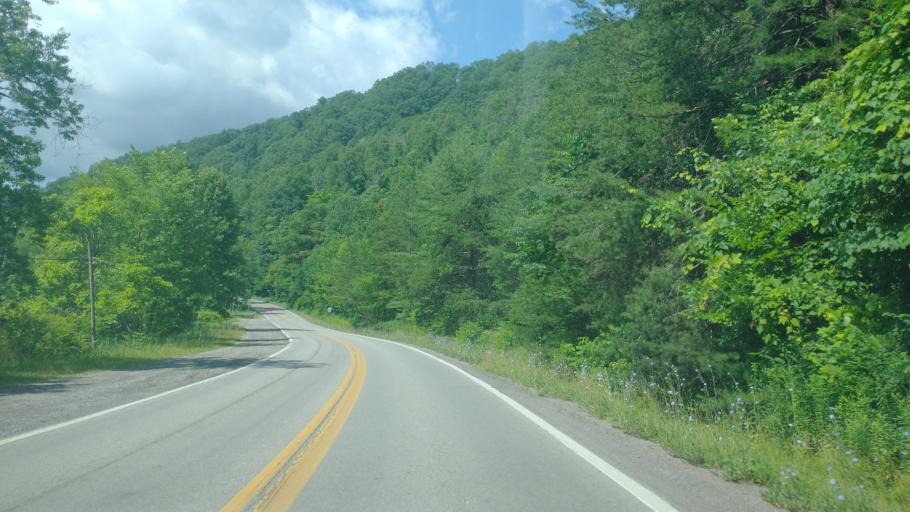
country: US
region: West Virginia
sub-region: McDowell County
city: Welch
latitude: 37.4290
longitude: -81.5096
